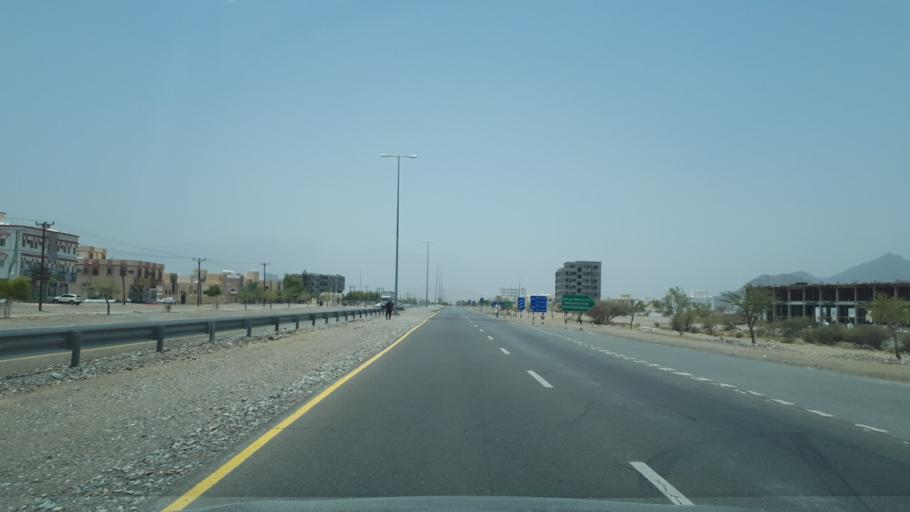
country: OM
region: Al Batinah
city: Rustaq
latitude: 23.4892
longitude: 57.4582
